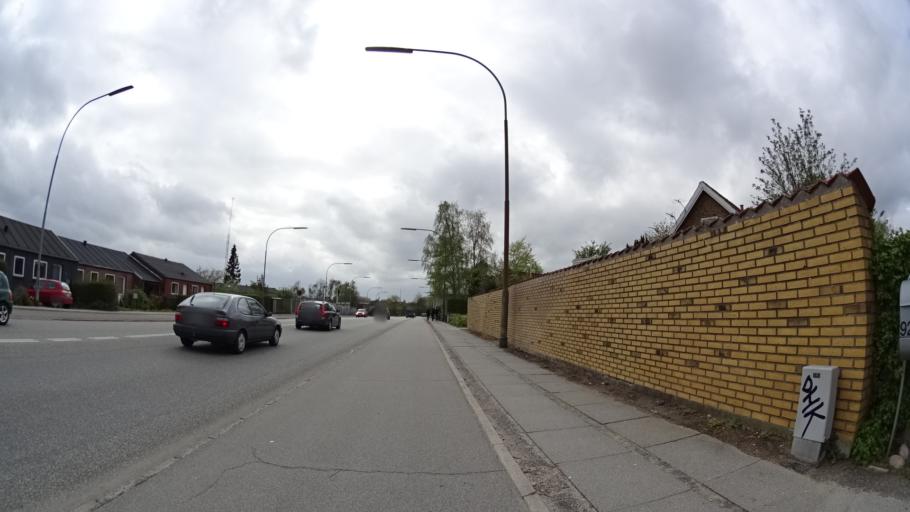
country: DK
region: Central Jutland
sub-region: Arhus Kommune
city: Stavtrup
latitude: 56.1470
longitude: 10.1550
